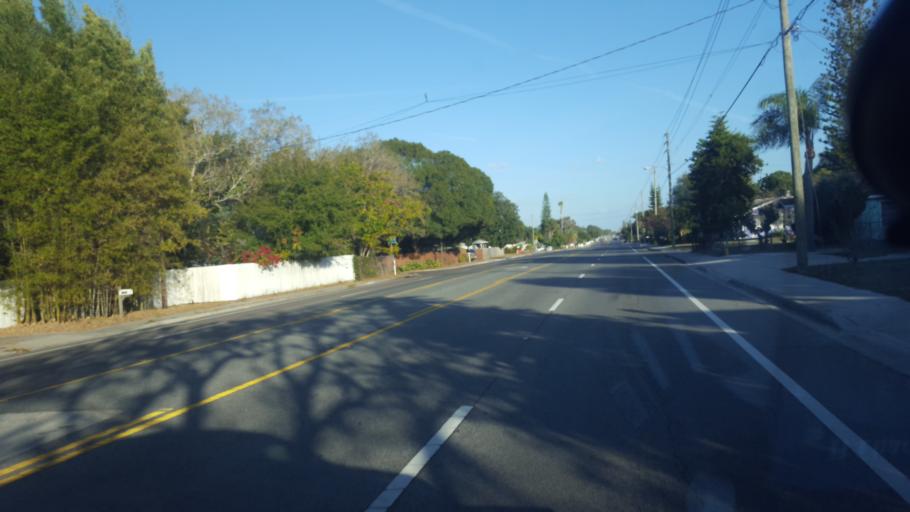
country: US
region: Florida
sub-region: Sarasota County
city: Southgate
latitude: 27.3228
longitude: -82.5115
